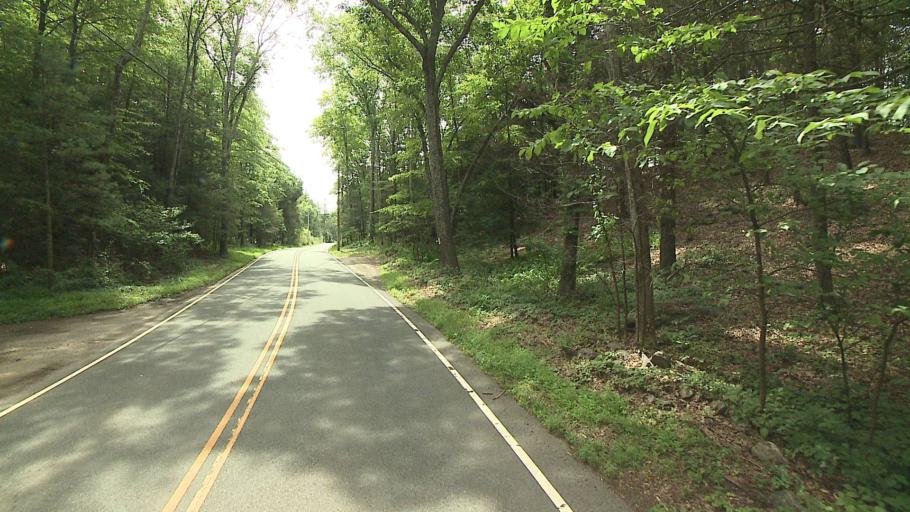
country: US
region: Connecticut
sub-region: Litchfield County
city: New Preston
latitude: 41.6001
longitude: -73.3220
